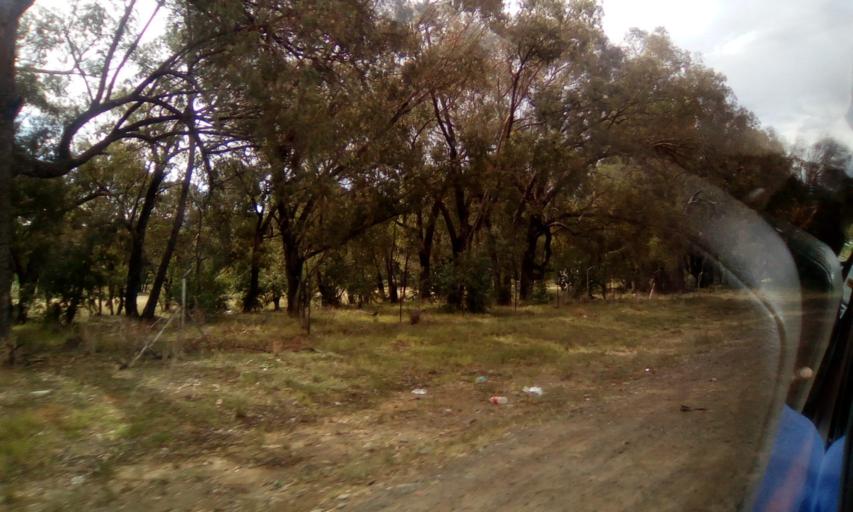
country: ZA
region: Orange Free State
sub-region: Thabo Mofutsanyana District Municipality
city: Ladybrand
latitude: -29.2037
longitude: 27.4663
